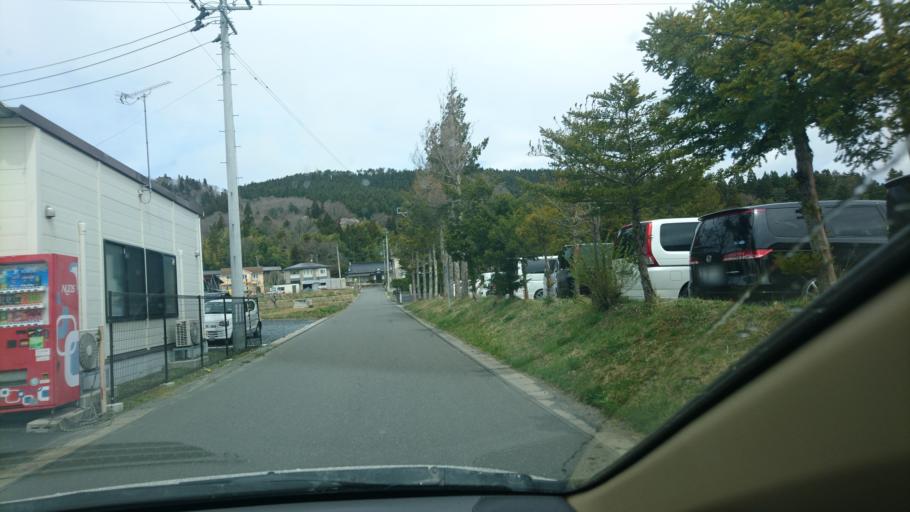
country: JP
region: Iwate
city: Ichinoseki
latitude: 38.9418
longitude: 141.0876
